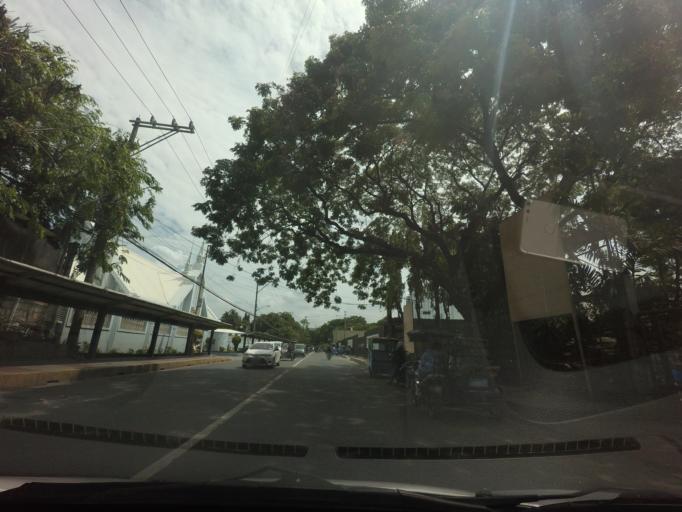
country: PH
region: Calabarzon
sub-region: Province of Rizal
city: Pateros
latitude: 14.5579
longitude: 121.0804
